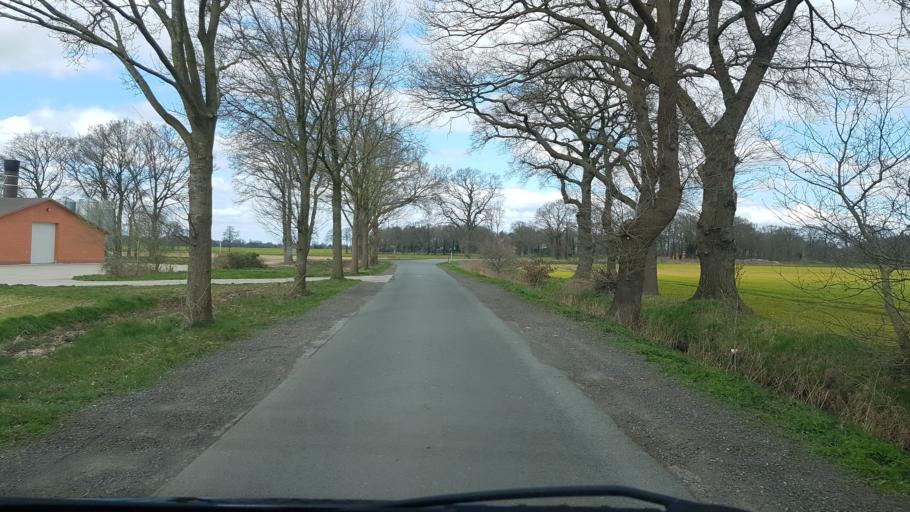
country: DE
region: Lower Saxony
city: Edewecht
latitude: 53.1089
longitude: 7.9429
